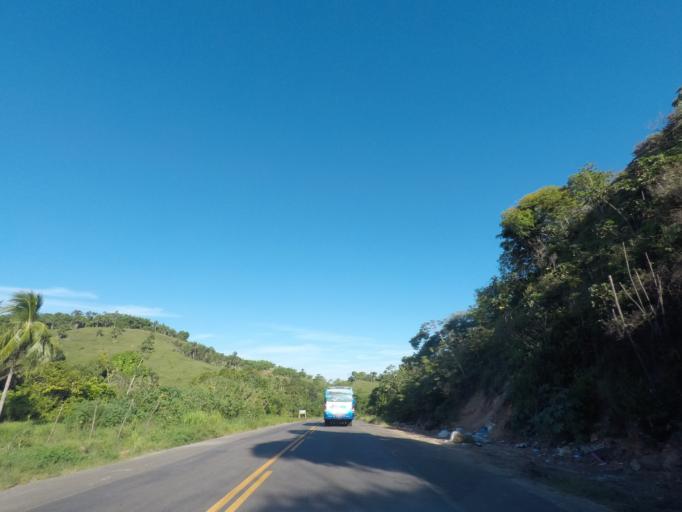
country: BR
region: Bahia
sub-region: Nazare
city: Nazare
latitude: -13.0288
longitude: -39.0099
